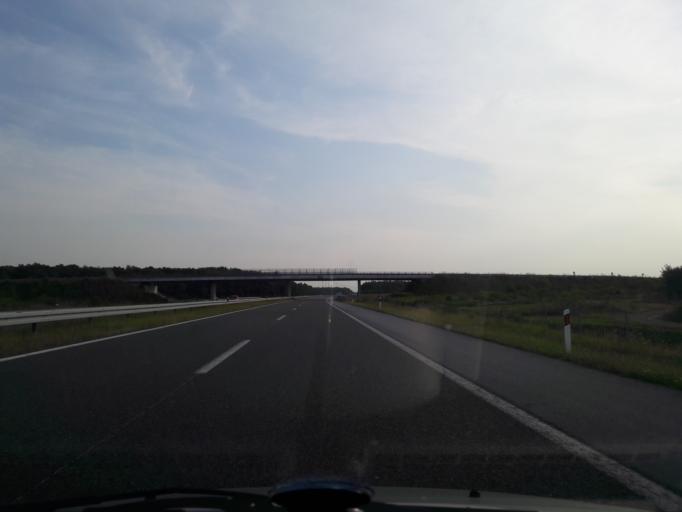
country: HR
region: Osjecko-Baranjska
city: Vuka
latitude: 45.4833
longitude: 18.4941
